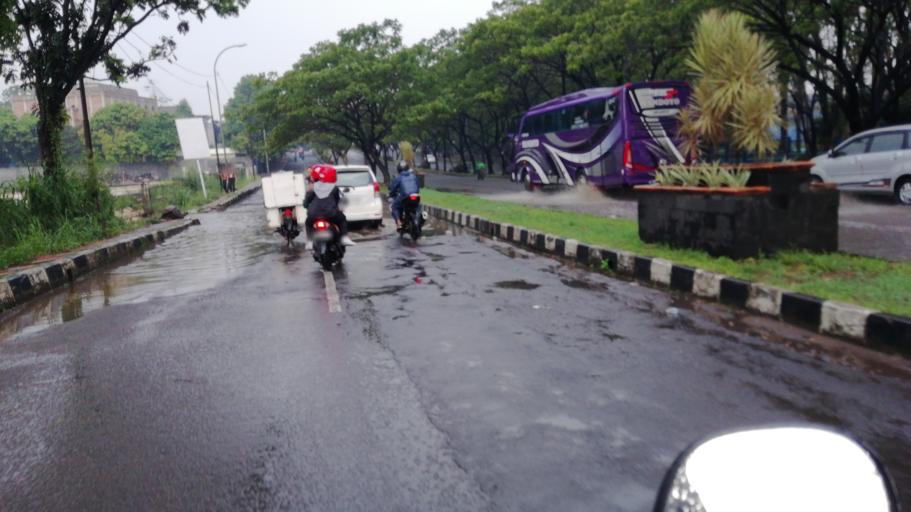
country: ID
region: West Java
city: Cibinong
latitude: -6.4822
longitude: 106.8154
